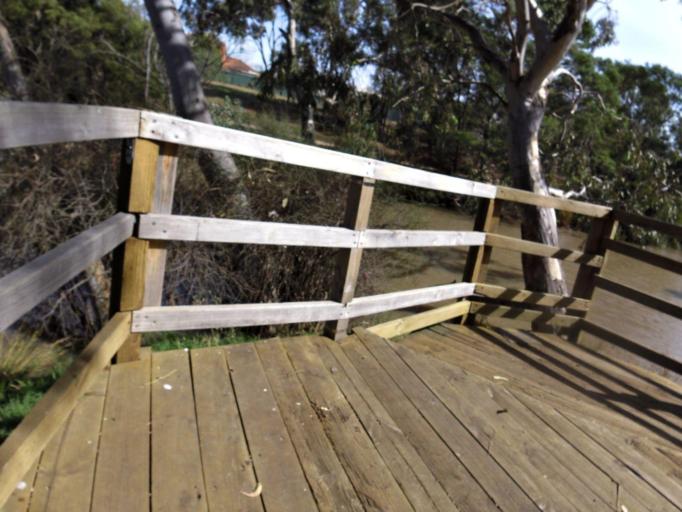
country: AU
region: Victoria
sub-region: Melton
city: Melton West
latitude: -37.6688
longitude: 144.5660
